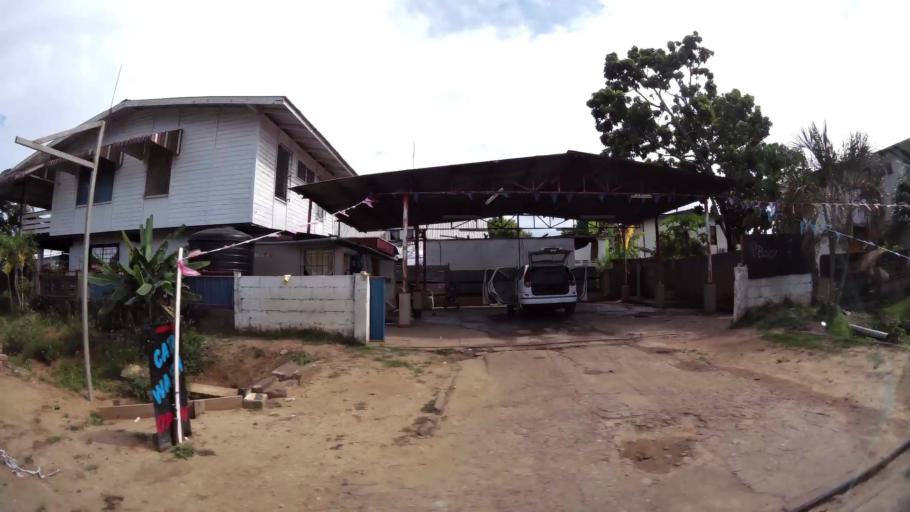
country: SR
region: Paramaribo
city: Paramaribo
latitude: 5.8446
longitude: -55.1470
